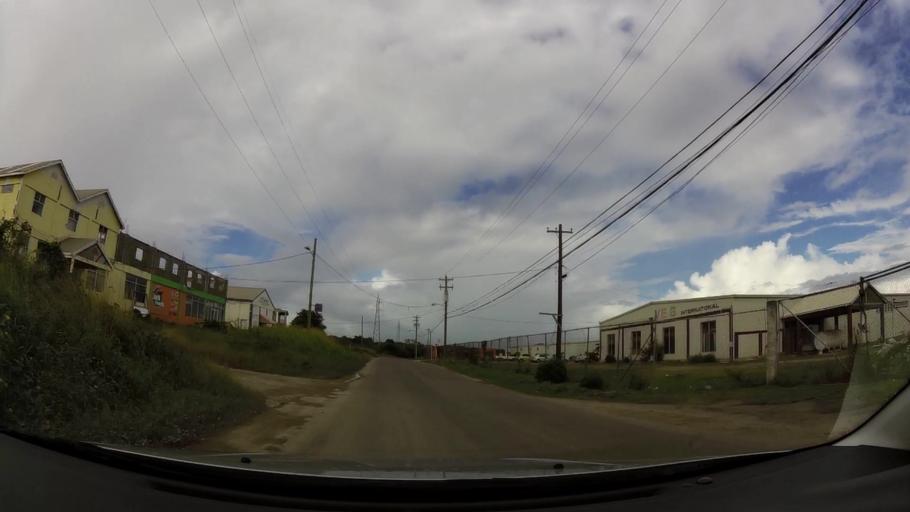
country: AG
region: Saint John
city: Potters Village
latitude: 17.0987
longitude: -61.8129
